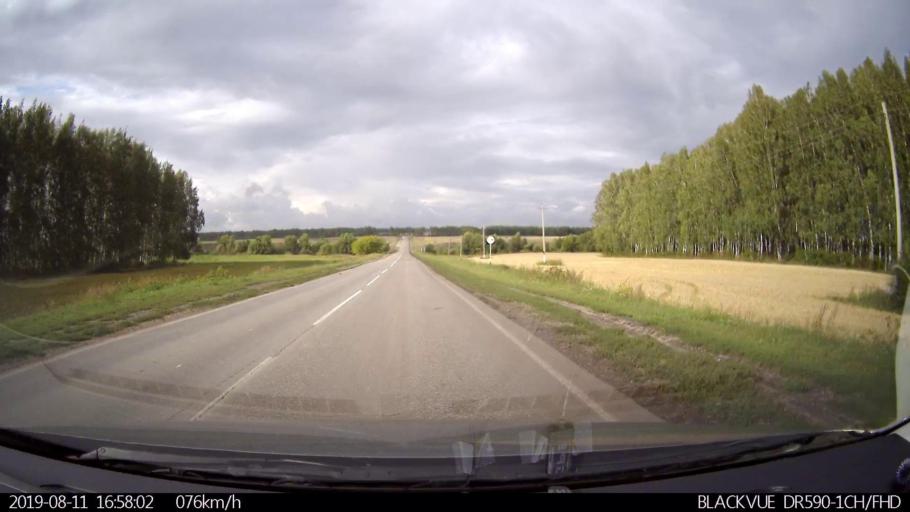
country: RU
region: Ulyanovsk
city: Mayna
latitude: 54.3043
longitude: 47.6550
